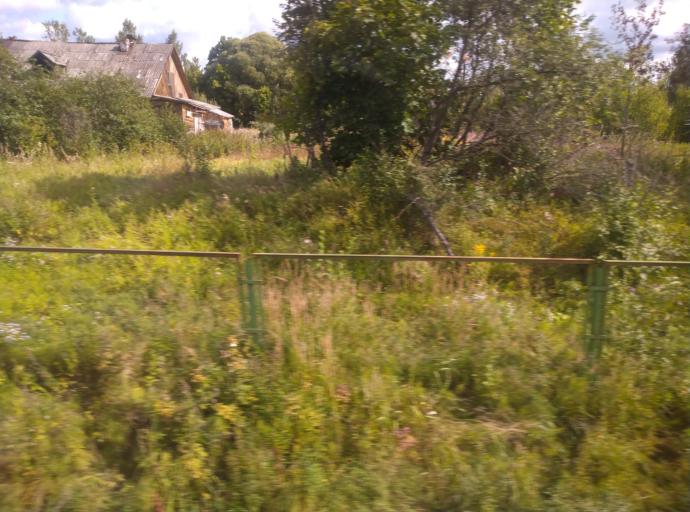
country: RU
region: Leningrad
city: Krasnyy Bor
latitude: 59.6827
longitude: 30.6980
